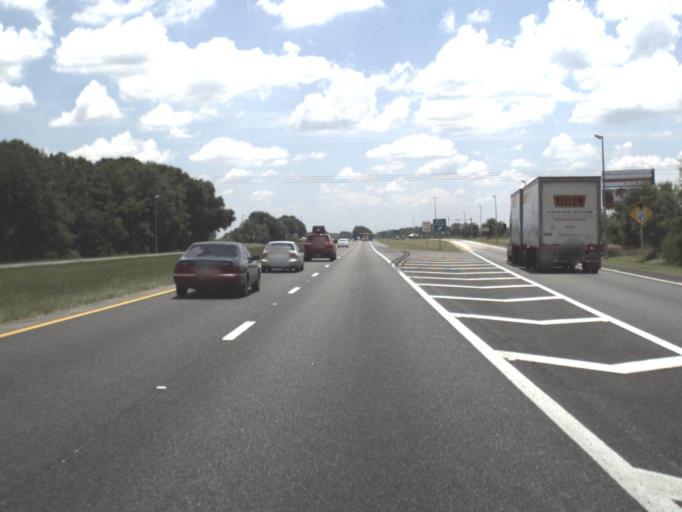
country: US
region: Florida
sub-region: Madison County
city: Madison
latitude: 30.3767
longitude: -83.2848
